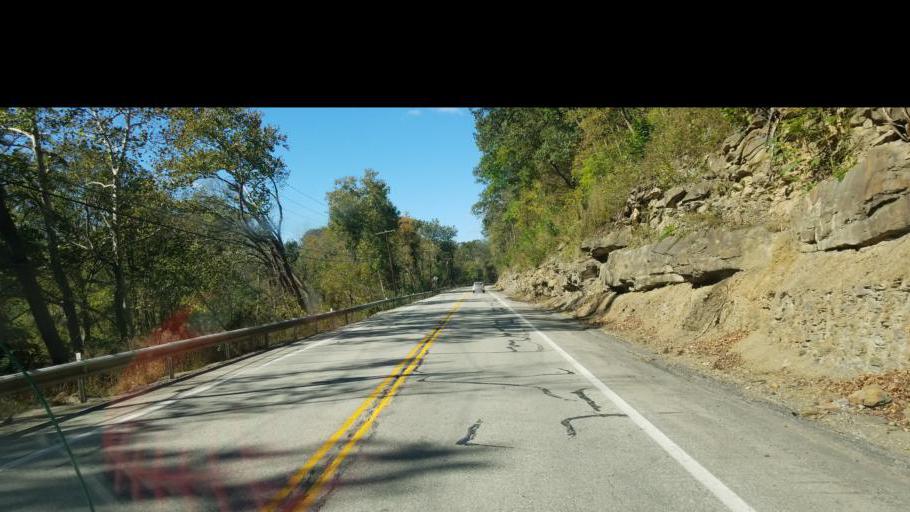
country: US
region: Pennsylvania
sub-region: Westmoreland County
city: Ligonier
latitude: 40.2319
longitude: -79.2239
